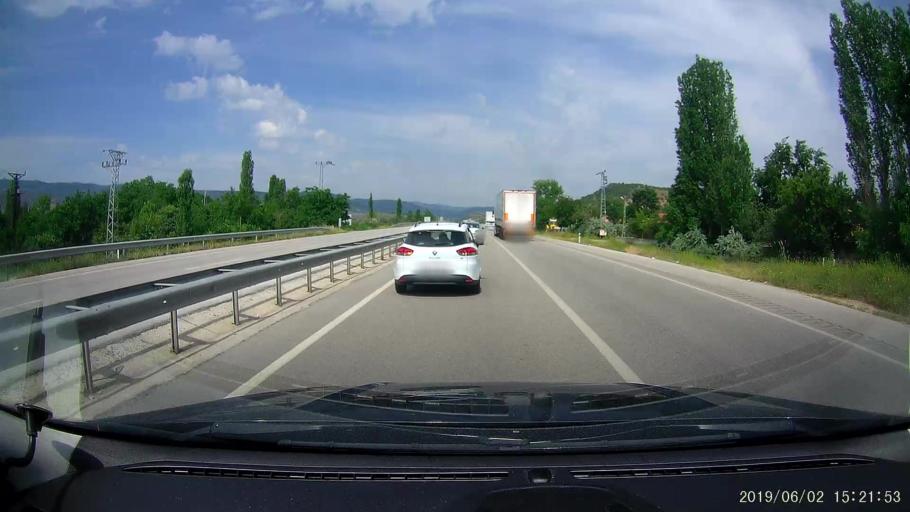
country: TR
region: Corum
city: Osmancik
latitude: 40.9788
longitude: 34.9459
